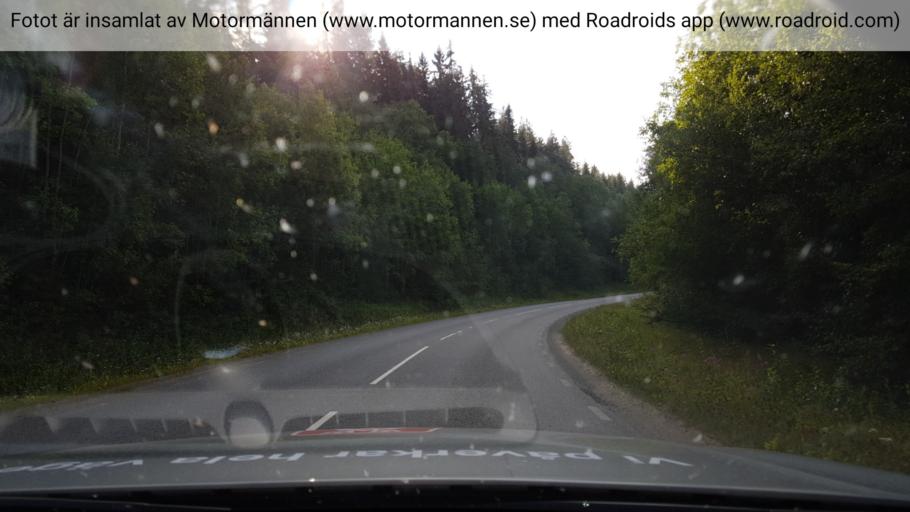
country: SE
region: Vaesternorrland
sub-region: Solleftea Kommun
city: As
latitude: 63.5794
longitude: 16.3445
